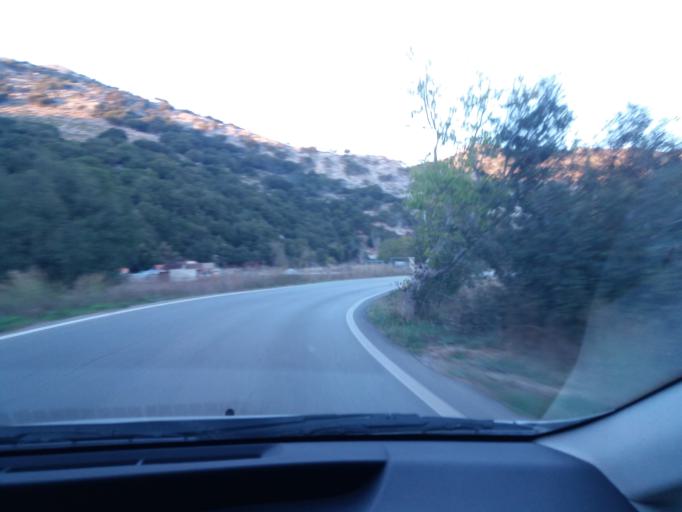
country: GR
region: Crete
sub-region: Nomos Irakleiou
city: Mokhos
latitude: 35.2033
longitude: 25.4745
